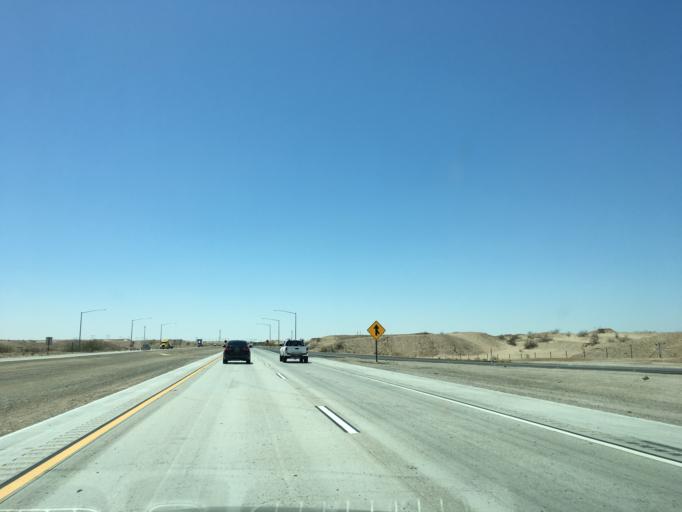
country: MX
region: Baja California
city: Los Algodones
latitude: 32.7437
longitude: -114.7210
